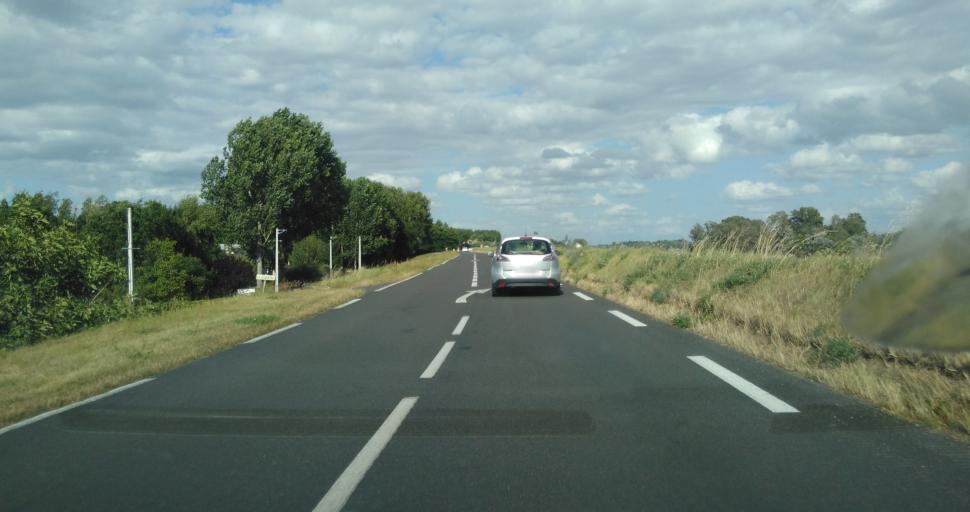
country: FR
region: Centre
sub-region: Departement d'Indre-et-Loire
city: La Chapelle-sur-Loire
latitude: 47.2423
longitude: 0.2044
